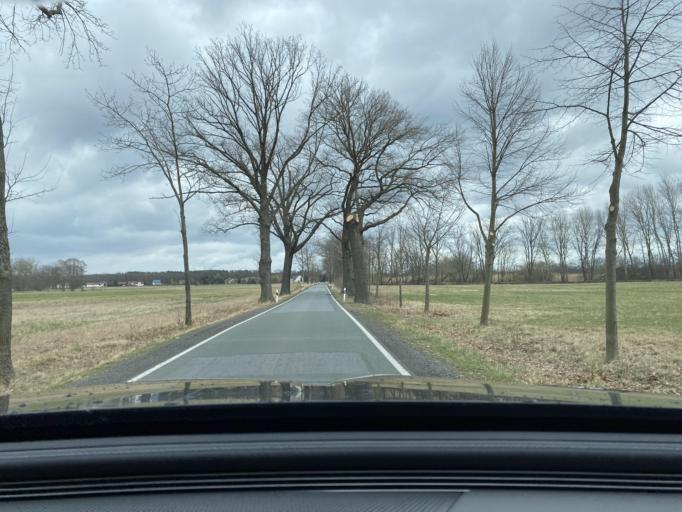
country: DE
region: Saxony
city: Uhyst
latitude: 51.3294
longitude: 14.4794
